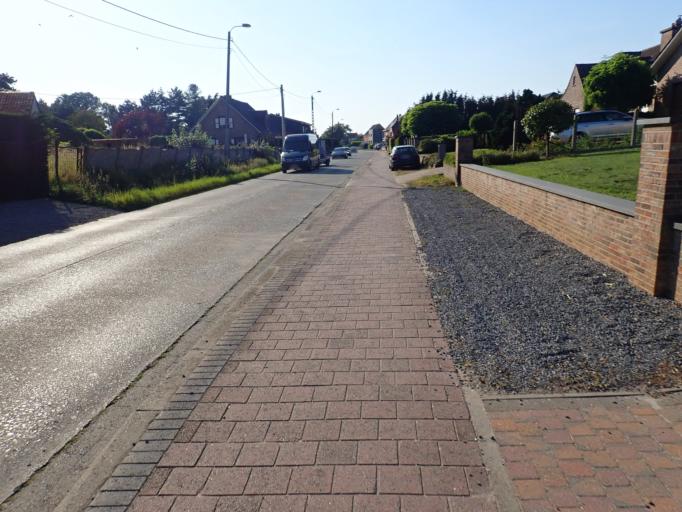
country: BE
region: Flanders
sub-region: Provincie Antwerpen
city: Heist-op-den-Berg
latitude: 51.1004
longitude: 4.7449
